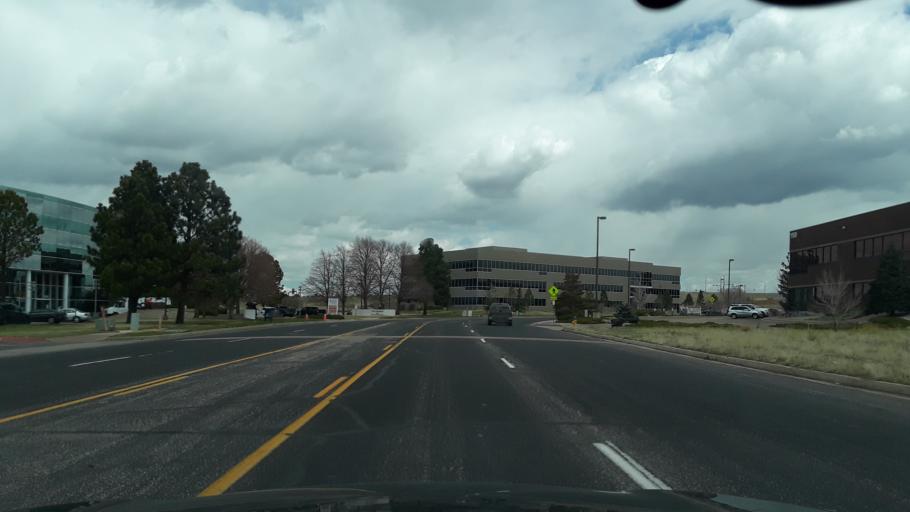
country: US
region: Colorado
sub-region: El Paso County
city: Air Force Academy
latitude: 38.9463
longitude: -104.8083
